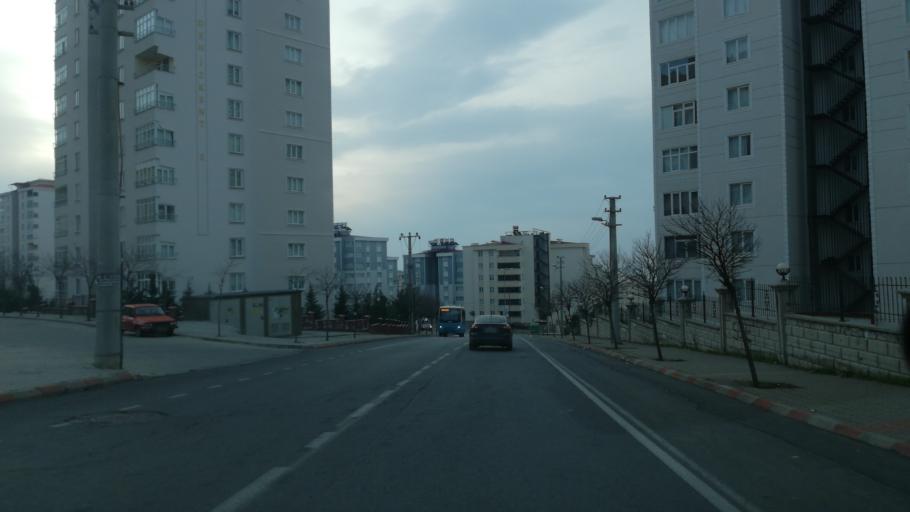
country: TR
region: Kahramanmaras
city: Kahramanmaras
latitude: 37.5985
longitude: 36.8913
